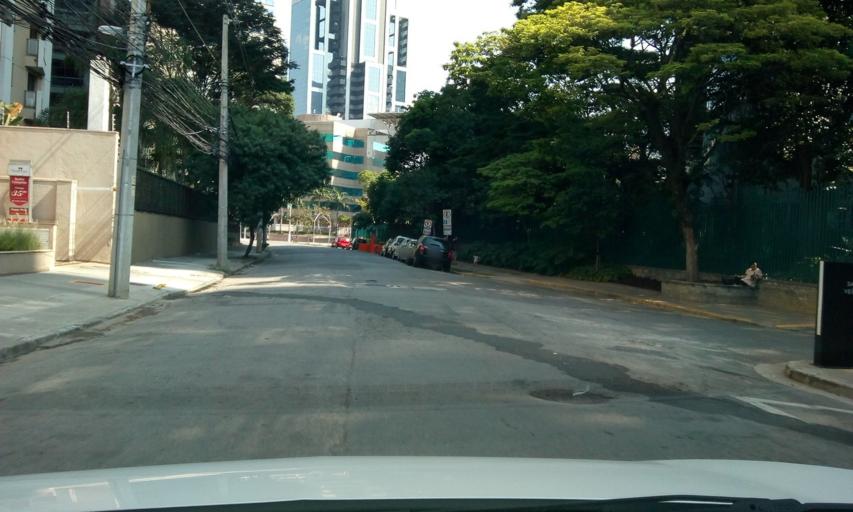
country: BR
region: Sao Paulo
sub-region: Sao Paulo
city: Sao Paulo
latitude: -23.5926
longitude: -46.6877
